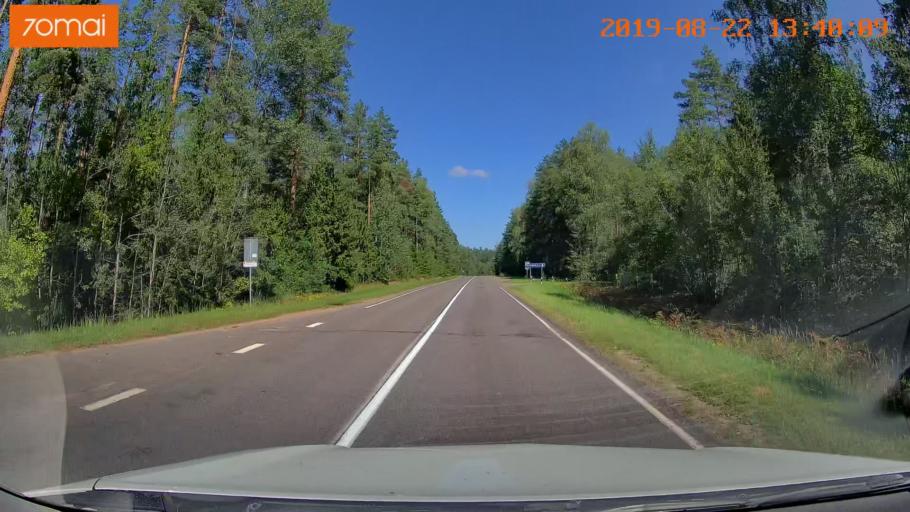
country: BY
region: Minsk
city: Staryya Darohi
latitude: 53.2338
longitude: 28.3618
